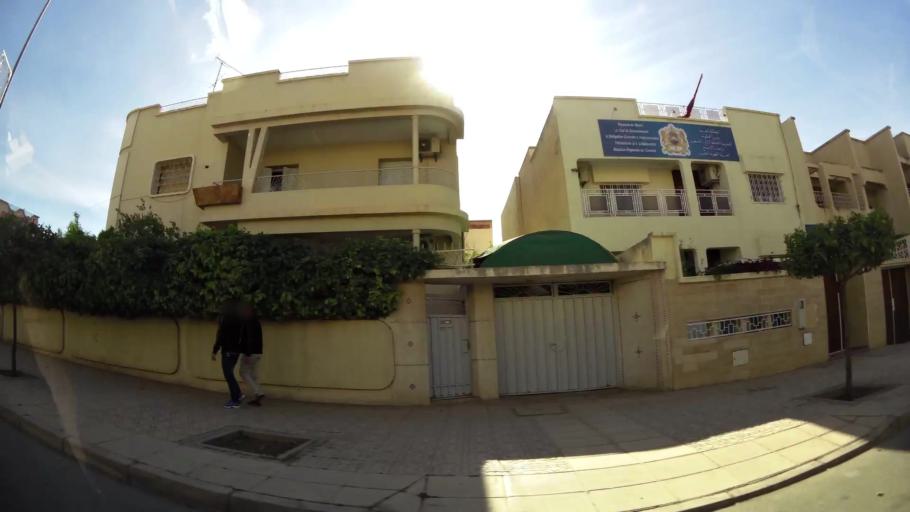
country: MA
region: Oriental
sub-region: Oujda-Angad
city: Oujda
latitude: 34.6702
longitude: -1.9064
